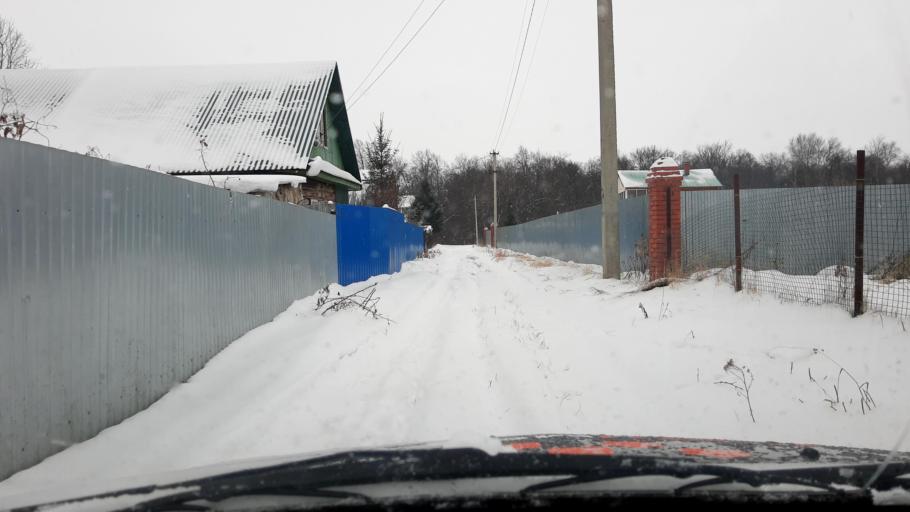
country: RU
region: Bashkortostan
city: Avdon
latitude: 54.4926
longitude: 55.8432
